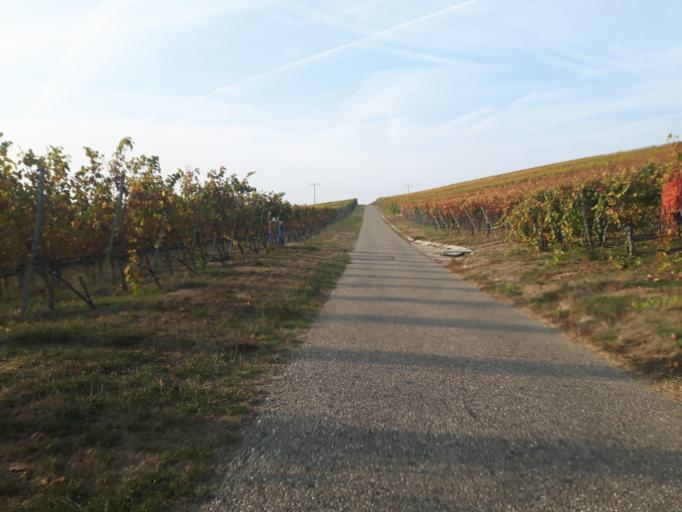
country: DE
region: Baden-Wuerttemberg
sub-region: Regierungsbezirk Stuttgart
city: Talheim
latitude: 49.0698
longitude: 9.1748
